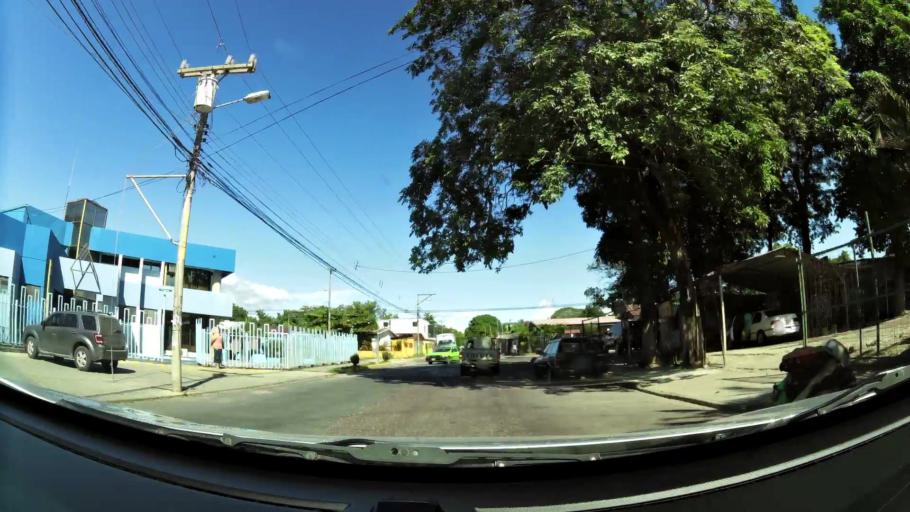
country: CR
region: Guanacaste
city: Liberia
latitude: 10.6344
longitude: -85.4392
